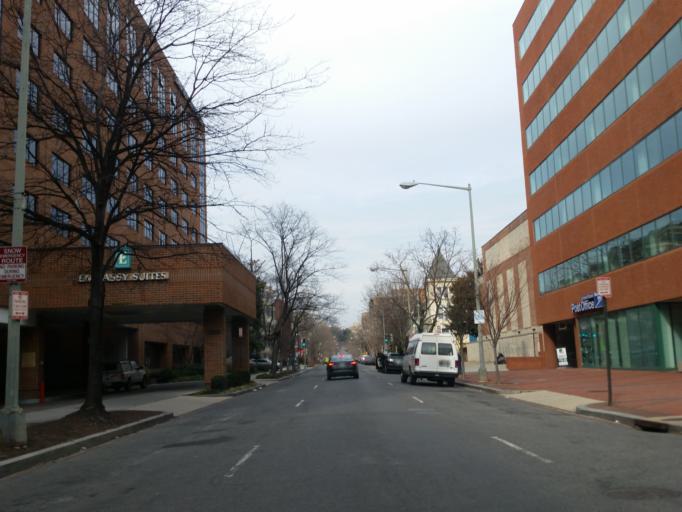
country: US
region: Washington, D.C.
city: Washington, D.C.
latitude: 38.9063
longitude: -77.0487
